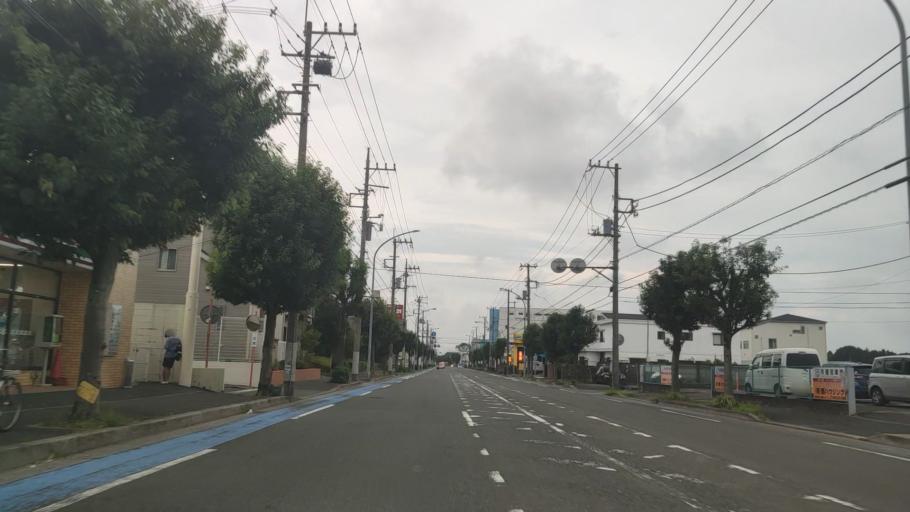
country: JP
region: Kanagawa
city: Fujisawa
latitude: 35.4133
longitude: 139.4848
